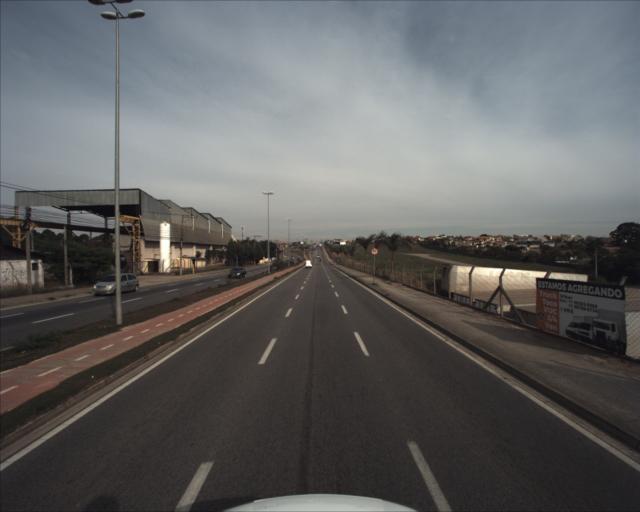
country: BR
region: Sao Paulo
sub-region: Sorocaba
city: Sorocaba
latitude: -23.4542
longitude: -47.4456
